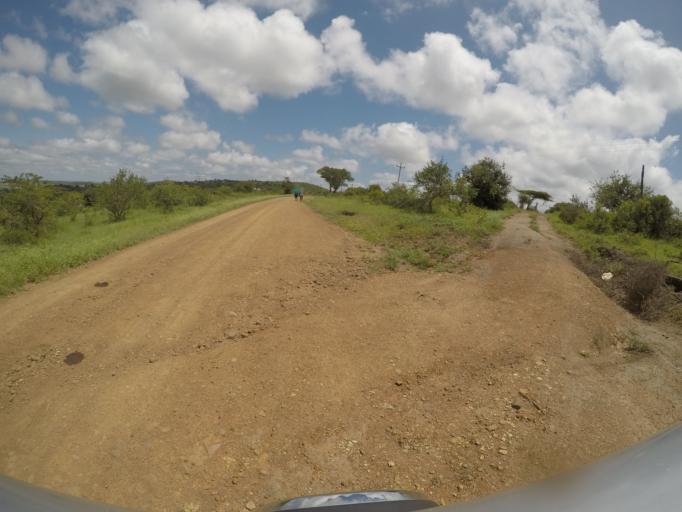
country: ZA
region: KwaZulu-Natal
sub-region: uThungulu District Municipality
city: Empangeni
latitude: -28.5855
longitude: 31.8254
